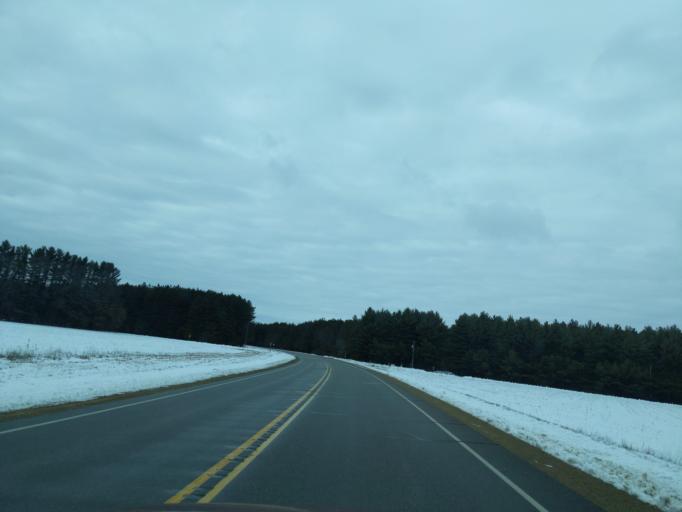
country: US
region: Wisconsin
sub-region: Waushara County
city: Wautoma
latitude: 43.9582
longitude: -89.3183
